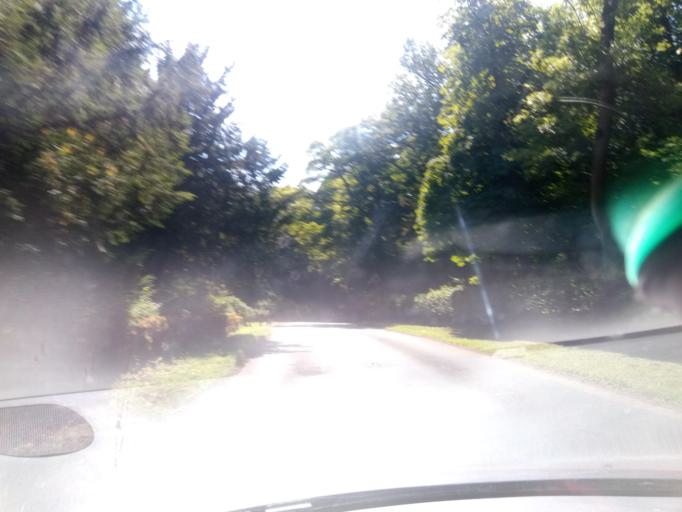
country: GB
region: England
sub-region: Northumberland
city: Bardon Mill
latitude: 54.9017
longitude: -2.3504
